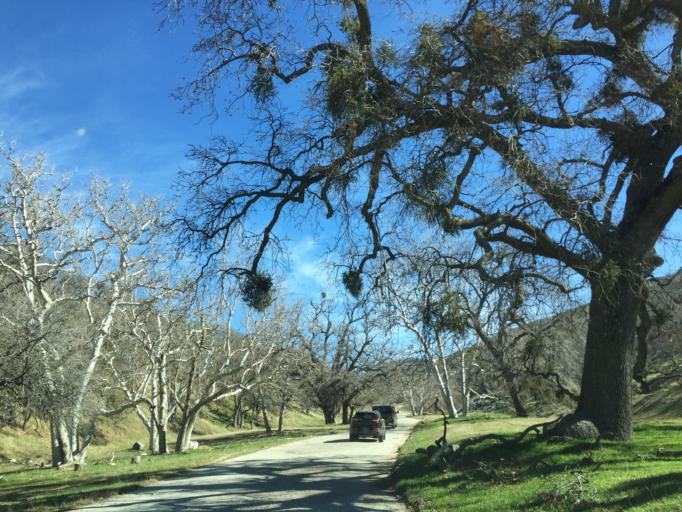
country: US
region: California
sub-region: Kern County
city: Lebec
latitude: 34.8840
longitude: -118.7736
